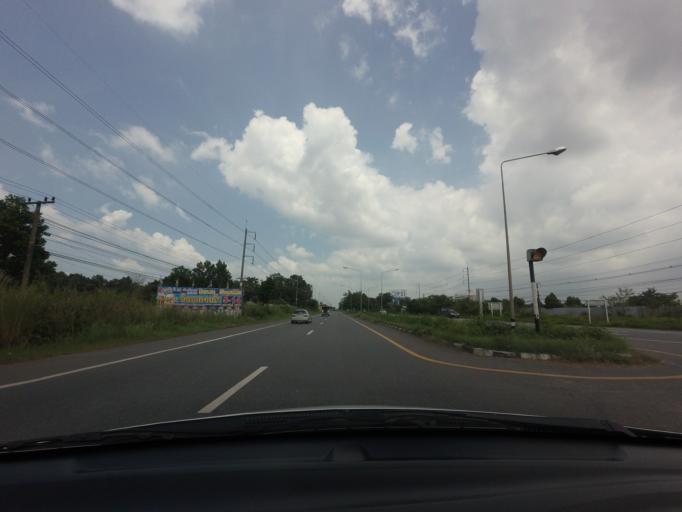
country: TH
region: Prachin Buri
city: Kabin Buri
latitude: 13.9554
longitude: 101.7222
